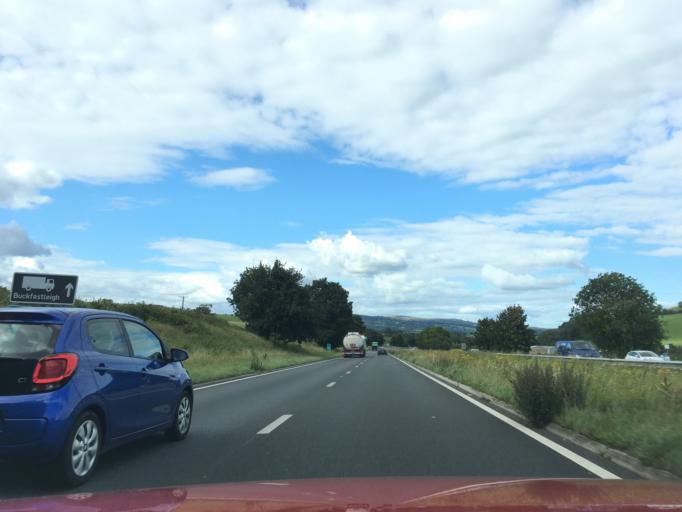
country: GB
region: England
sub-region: Devon
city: Buckfastleigh
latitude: 50.4630
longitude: -3.7901
